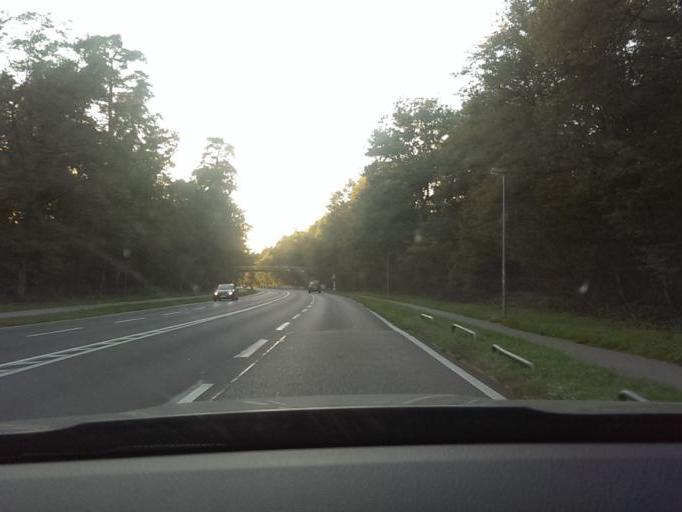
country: DE
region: Baden-Wuerttemberg
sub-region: Karlsruhe Region
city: Karlsruhe
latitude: 49.0238
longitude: 8.4080
